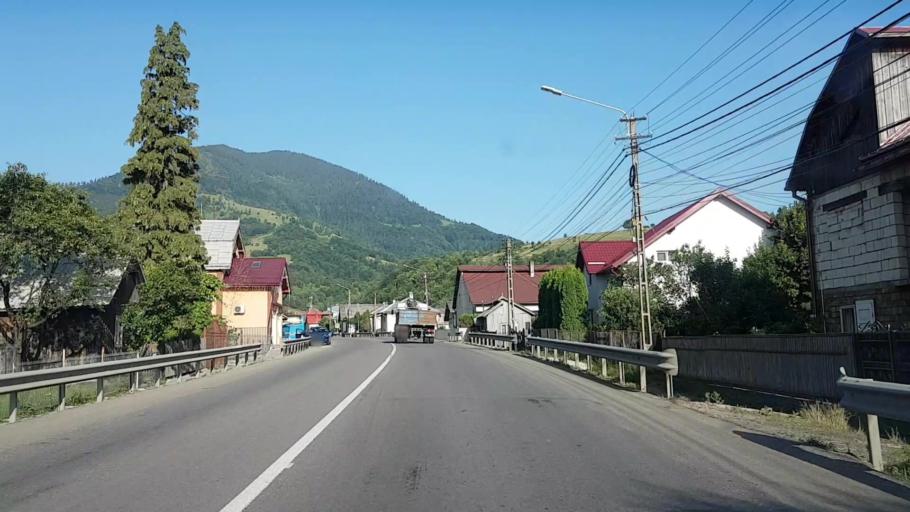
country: RO
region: Bistrita-Nasaud
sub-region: Comuna Tiha Bargaului
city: Tureac
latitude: 47.2108
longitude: 24.8562
